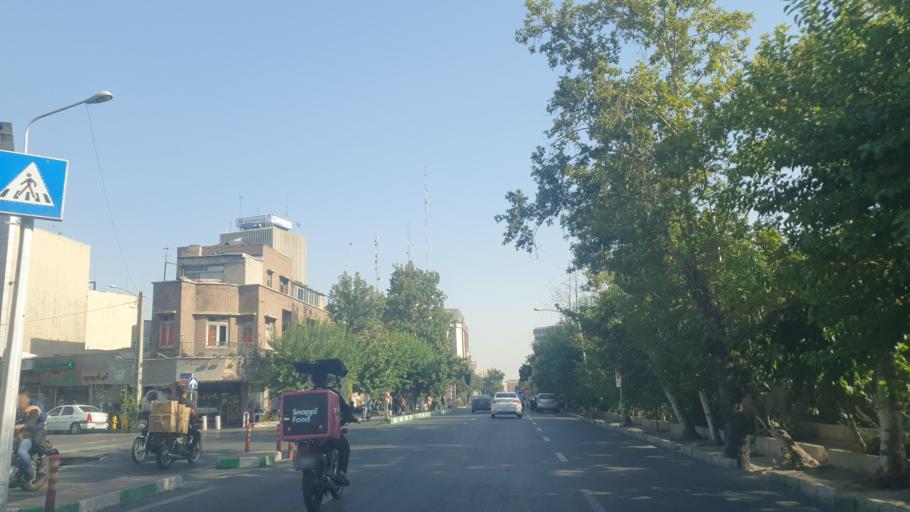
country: IR
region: Tehran
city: Tehran
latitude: 35.7098
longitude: 51.4255
